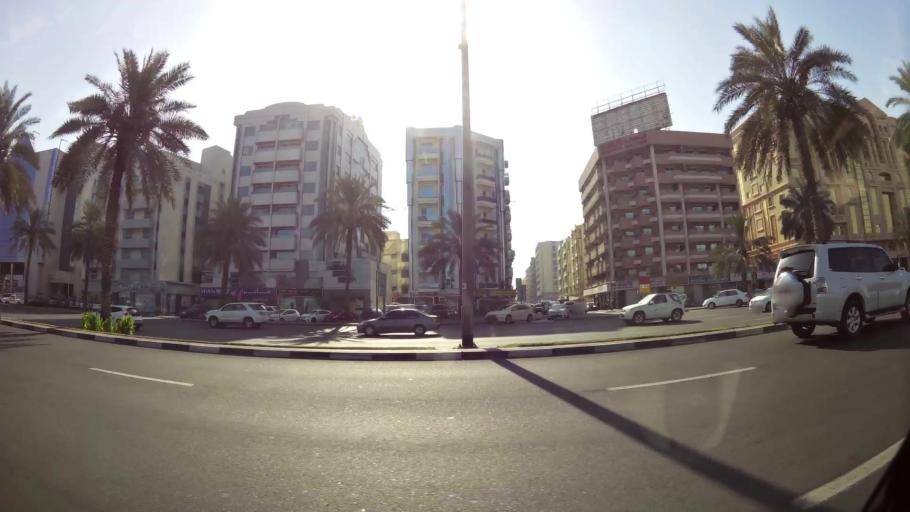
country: AE
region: Ash Shariqah
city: Sharjah
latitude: 25.2575
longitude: 55.2847
